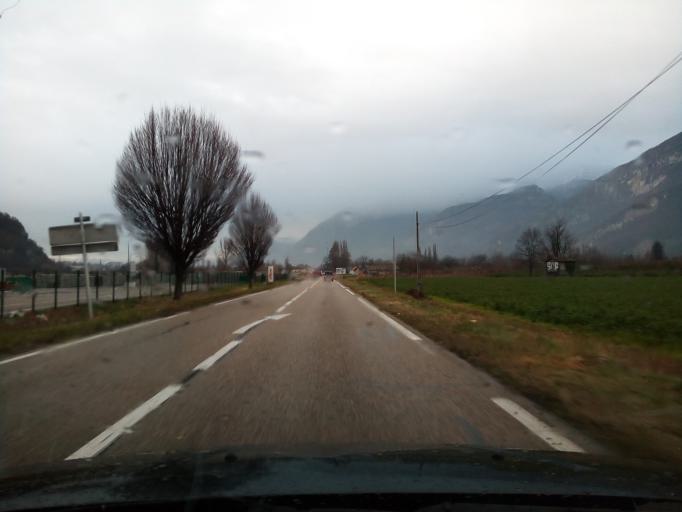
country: FR
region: Rhone-Alpes
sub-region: Departement de l'Isere
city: Voreppe
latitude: 45.3113
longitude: 5.6225
